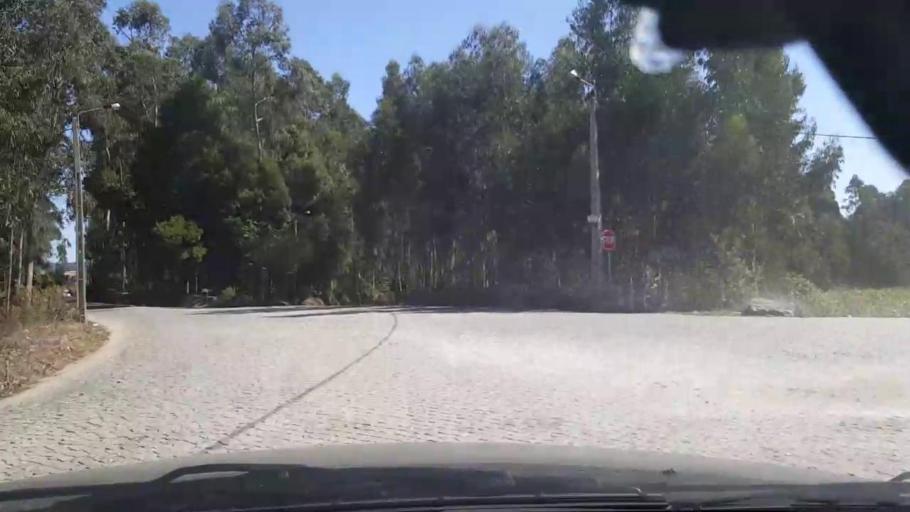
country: PT
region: Porto
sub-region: Vila do Conde
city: Arvore
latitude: 41.3118
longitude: -8.6856
